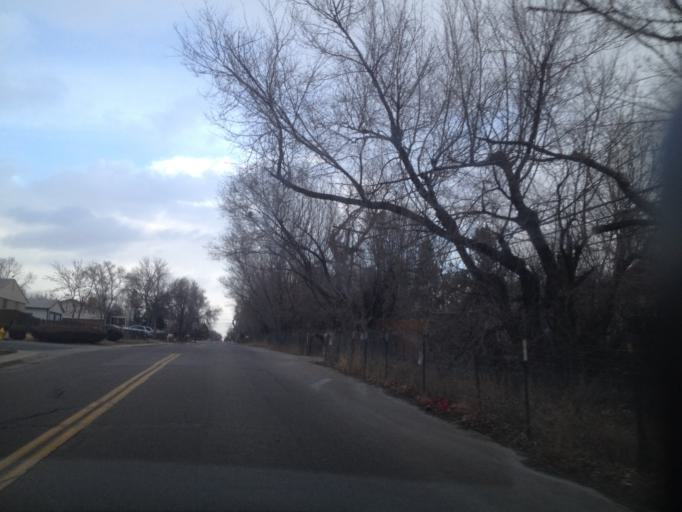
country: US
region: Colorado
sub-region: Adams County
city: Berkley
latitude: 39.8072
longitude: -105.0441
